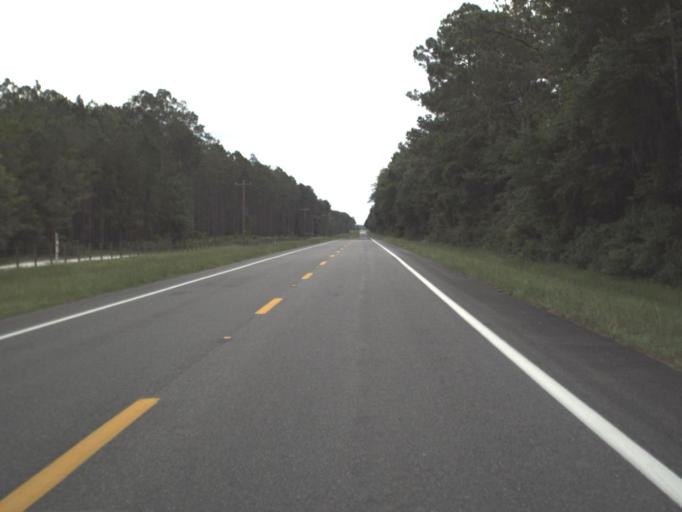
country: US
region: Florida
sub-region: Union County
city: Lake Butler
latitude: 30.0446
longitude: -82.3923
